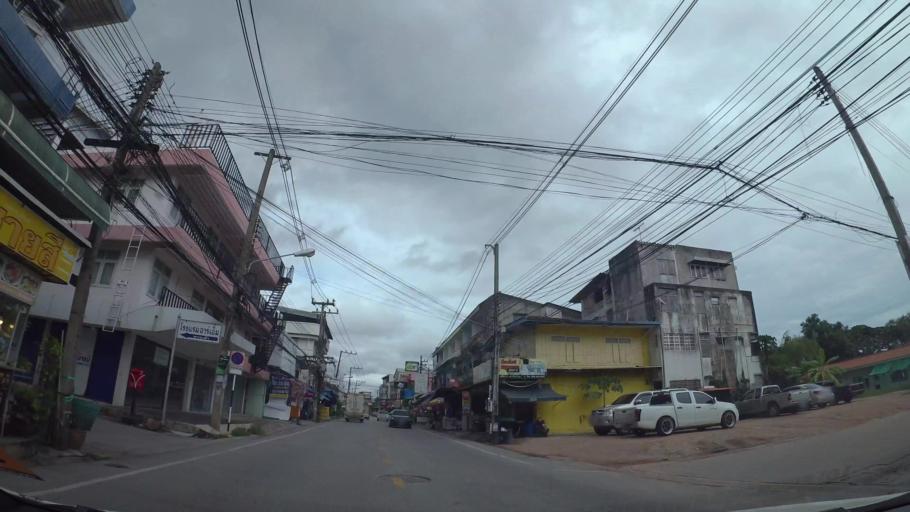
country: TH
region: Rayong
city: Rayong
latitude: 12.6801
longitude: 101.2626
